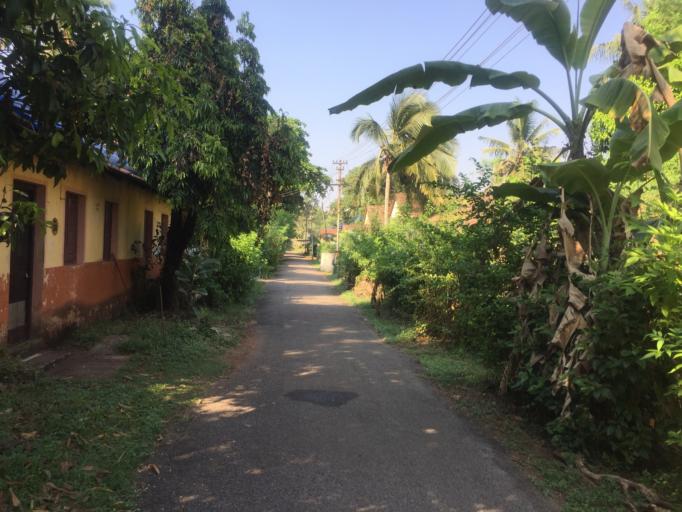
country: IN
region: Karnataka
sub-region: Dakshina Kannada
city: Ullal
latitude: 12.8624
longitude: 74.8417
